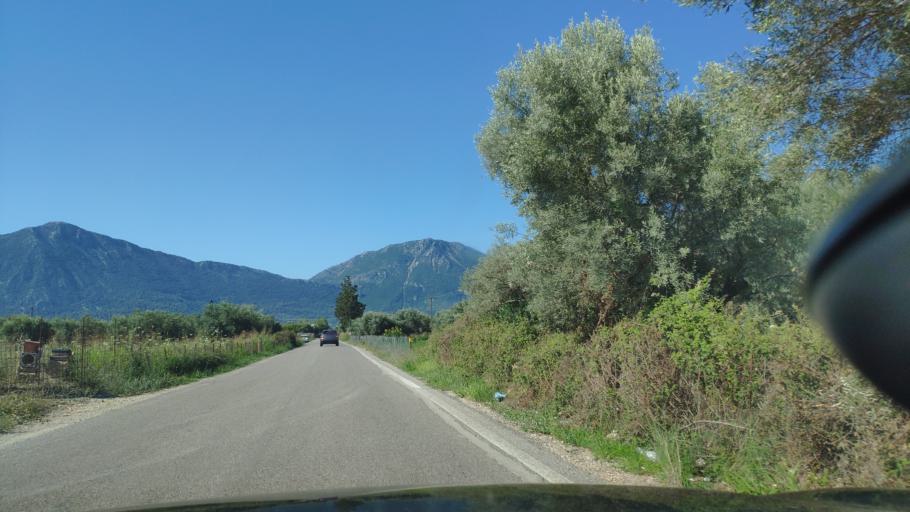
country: GR
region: West Greece
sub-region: Nomos Aitolias kai Akarnanias
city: Kandila
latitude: 38.6861
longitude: 20.9438
